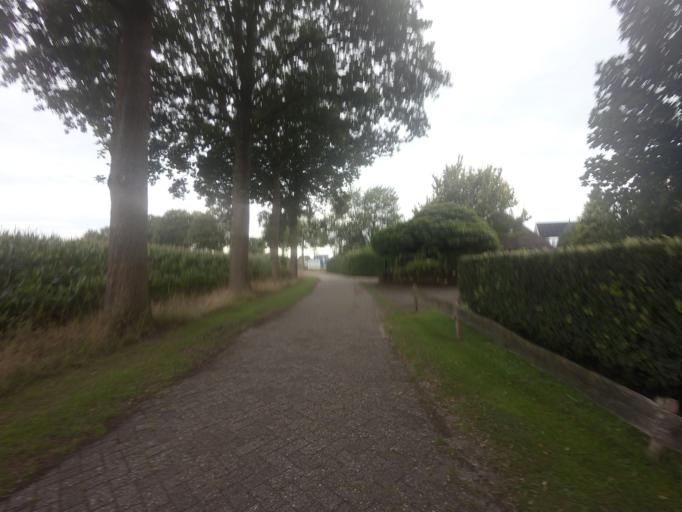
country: NL
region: Overijssel
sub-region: Gemeente Raalte
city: Raalte
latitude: 52.3322
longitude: 6.2898
